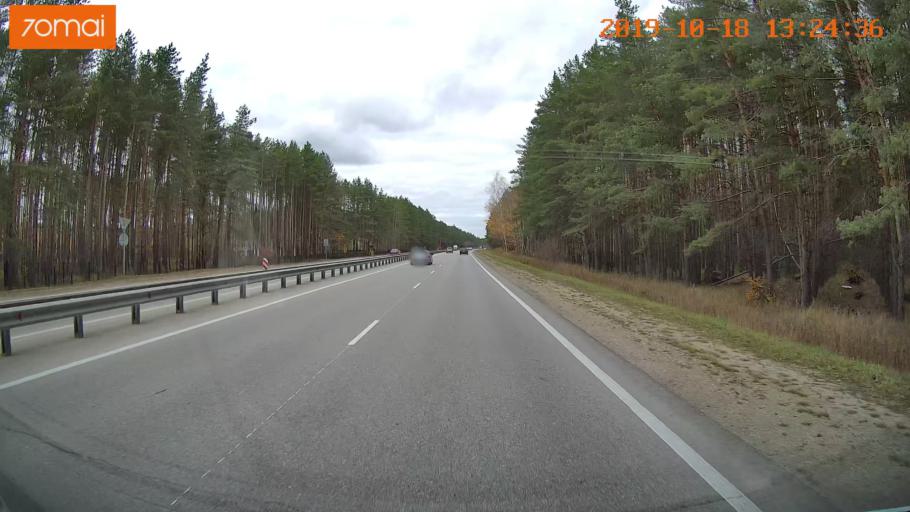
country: RU
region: Rjazan
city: Polyany
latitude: 54.7330
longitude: 39.8429
